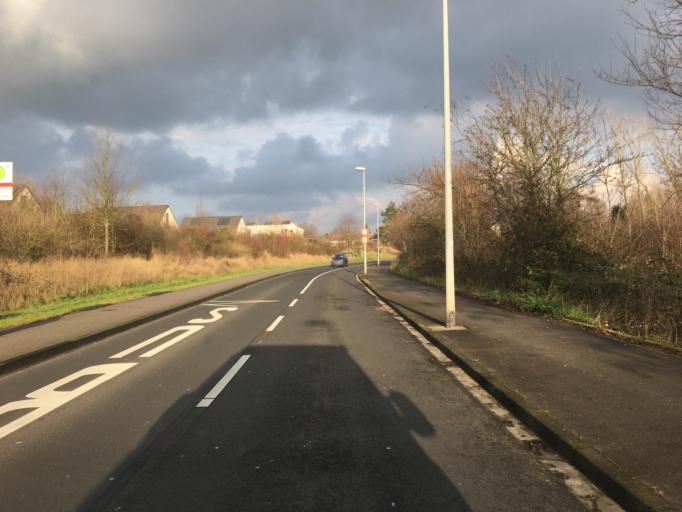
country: DE
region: North Rhine-Westphalia
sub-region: Regierungsbezirk Dusseldorf
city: Dormagen
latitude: 51.0558
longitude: 6.8548
